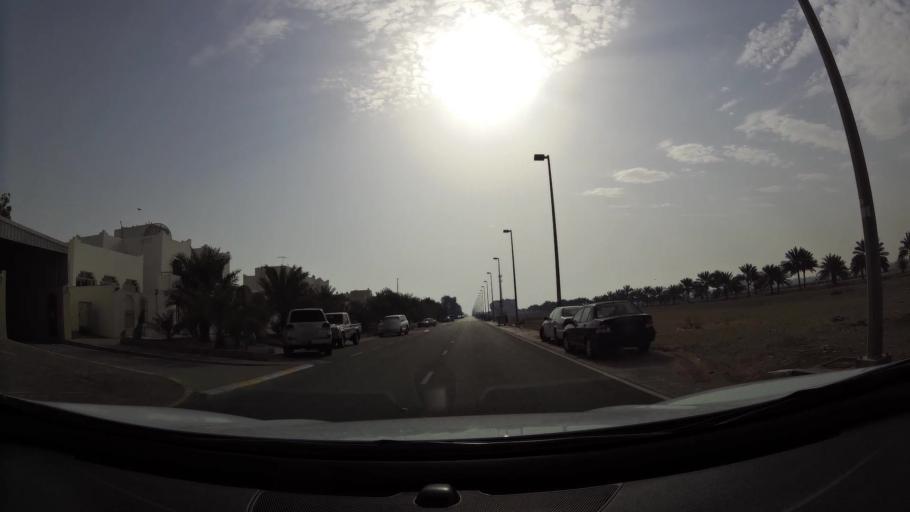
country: AE
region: Abu Dhabi
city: Abu Dhabi
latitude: 24.2414
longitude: 54.7142
